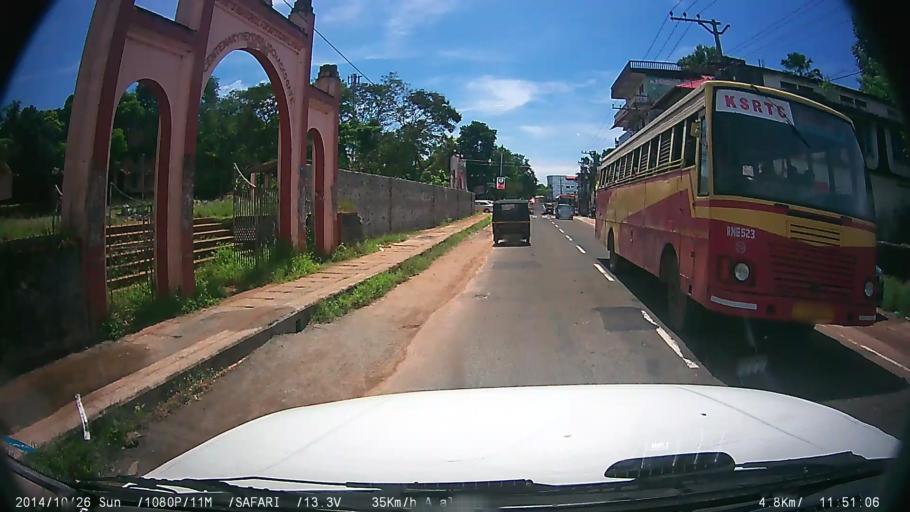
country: IN
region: Kerala
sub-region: Kottayam
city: Palackattumala
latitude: 9.7566
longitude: 76.5612
